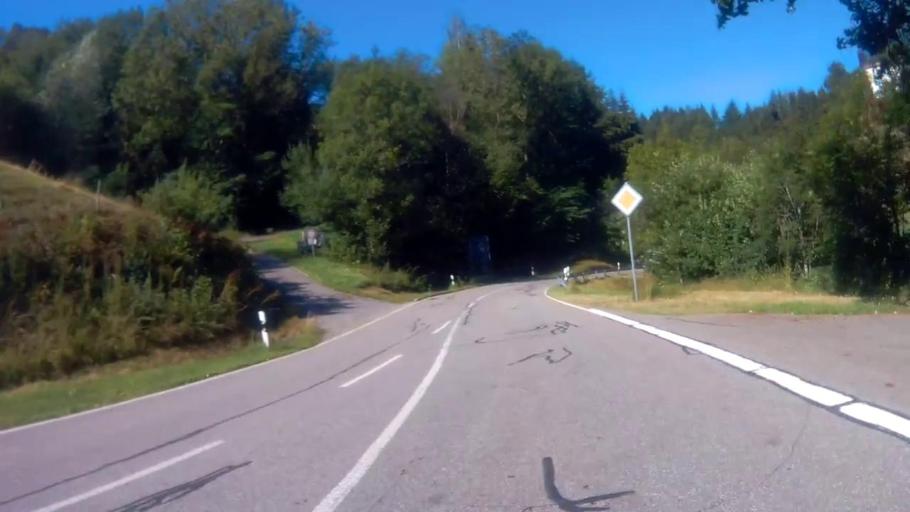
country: DE
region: Baden-Wuerttemberg
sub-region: Freiburg Region
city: Wembach
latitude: 47.7318
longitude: 7.9186
